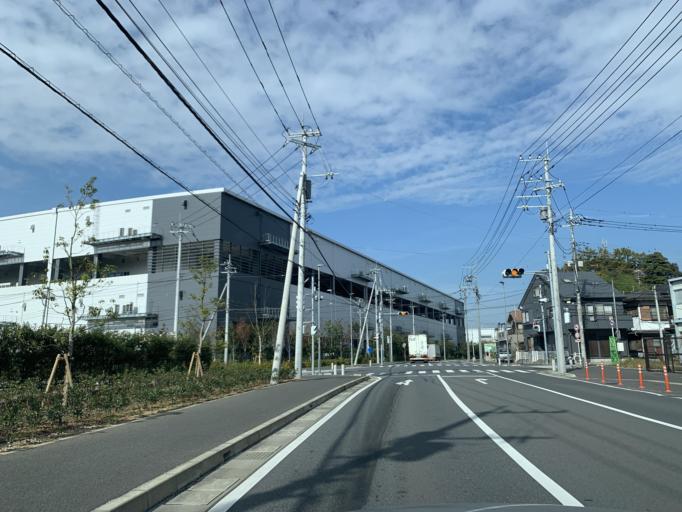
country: JP
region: Chiba
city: Nagareyama
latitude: 35.9050
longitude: 139.8933
